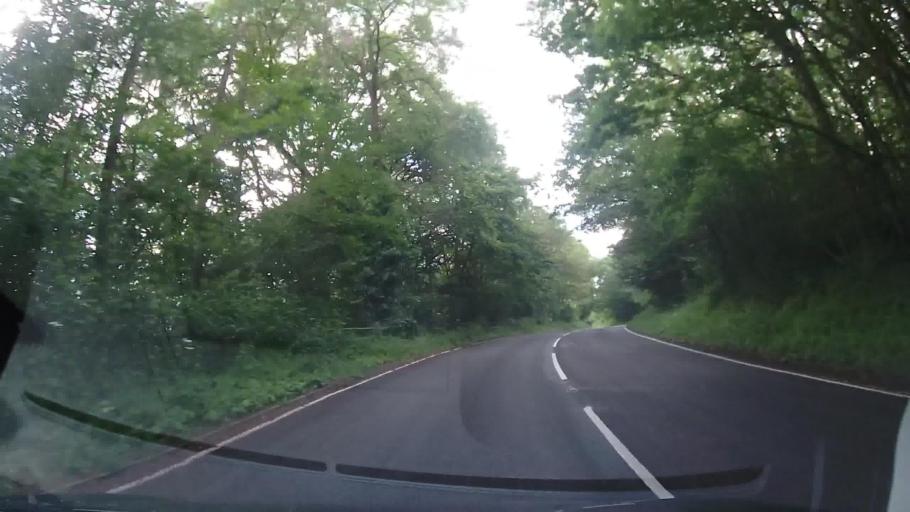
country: GB
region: England
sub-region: Shropshire
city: Much Wenlock
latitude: 52.6416
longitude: -2.5671
